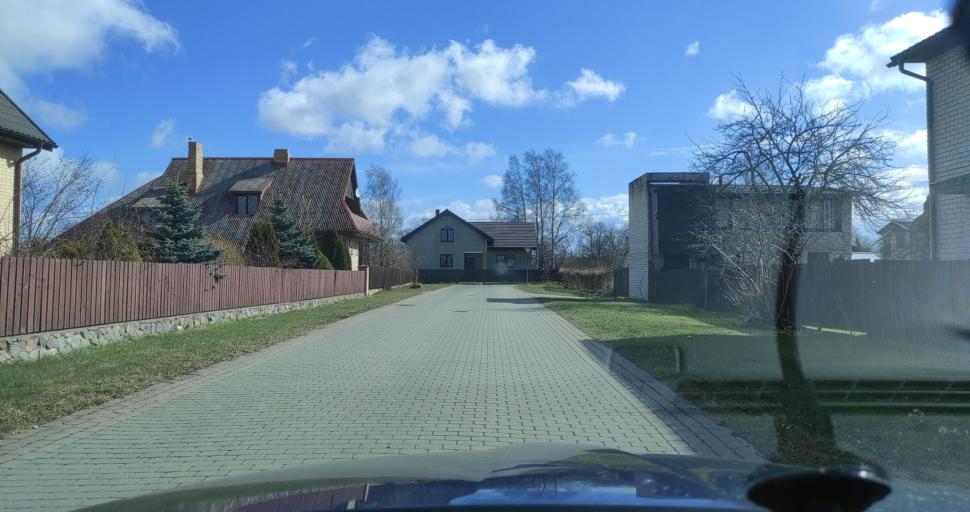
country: LV
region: Ventspils
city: Ventspils
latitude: 57.3778
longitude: 21.5696
